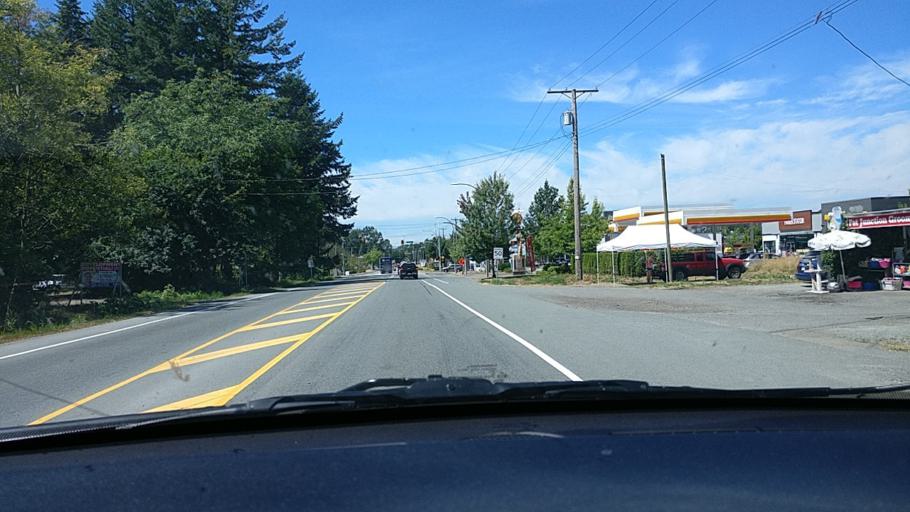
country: CA
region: British Columbia
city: Aldergrove
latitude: 49.0576
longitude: -122.4578
